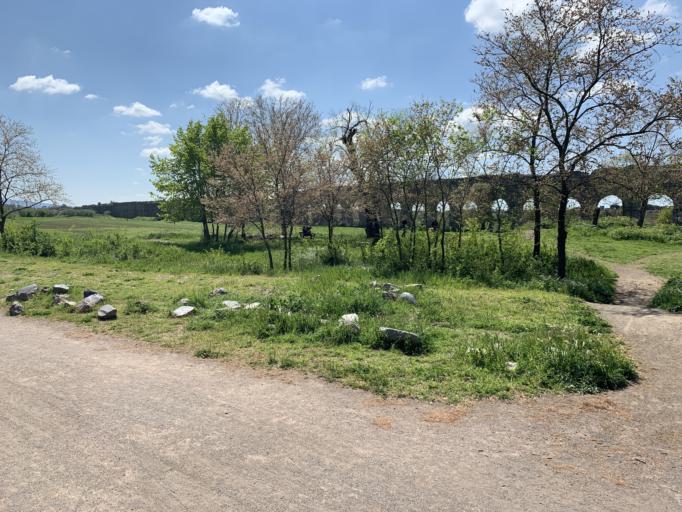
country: IT
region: Latium
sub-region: Citta metropolitana di Roma Capitale
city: Ciampino
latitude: 41.8465
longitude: 12.5627
